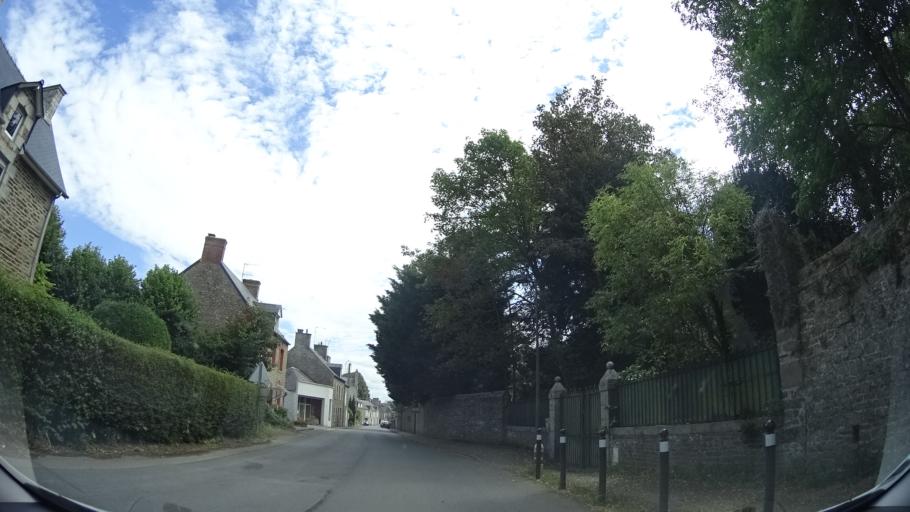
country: FR
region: Lower Normandy
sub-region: Departement de la Manche
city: Sartilly
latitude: 48.6858
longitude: -1.4798
